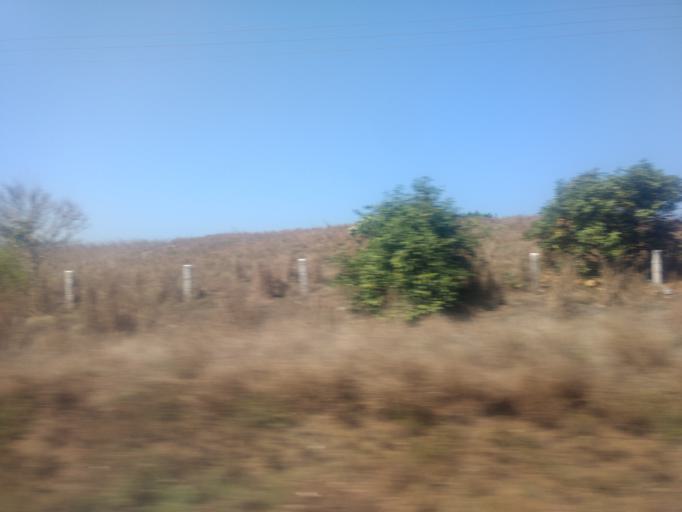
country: MX
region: Colima
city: Armeria
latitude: 18.9490
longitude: -104.1235
